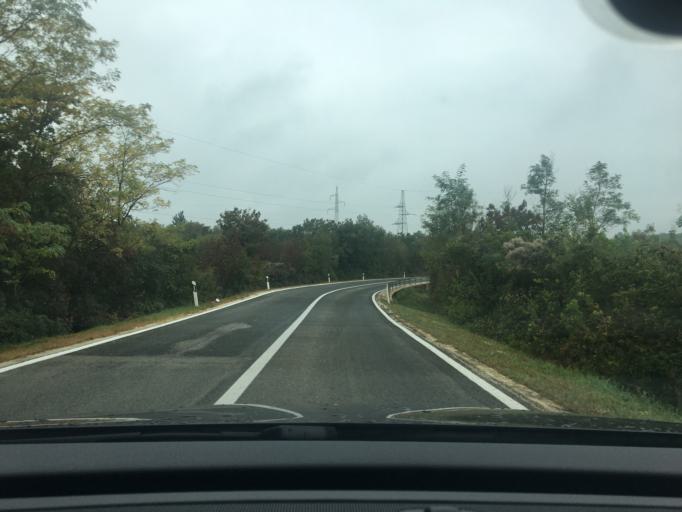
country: HR
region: Istarska
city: Buje
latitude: 45.4235
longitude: 13.6603
